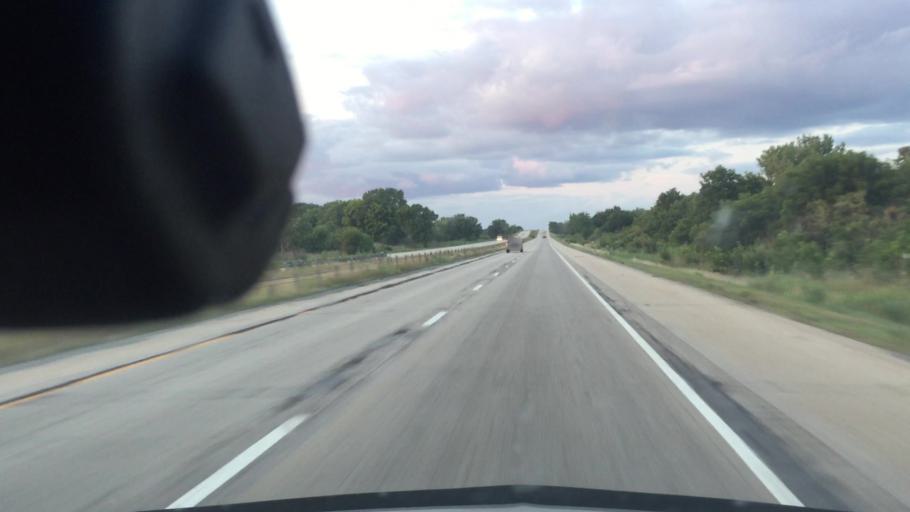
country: US
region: Illinois
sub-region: Grundy County
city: Central City
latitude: 41.2155
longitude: -88.2901
